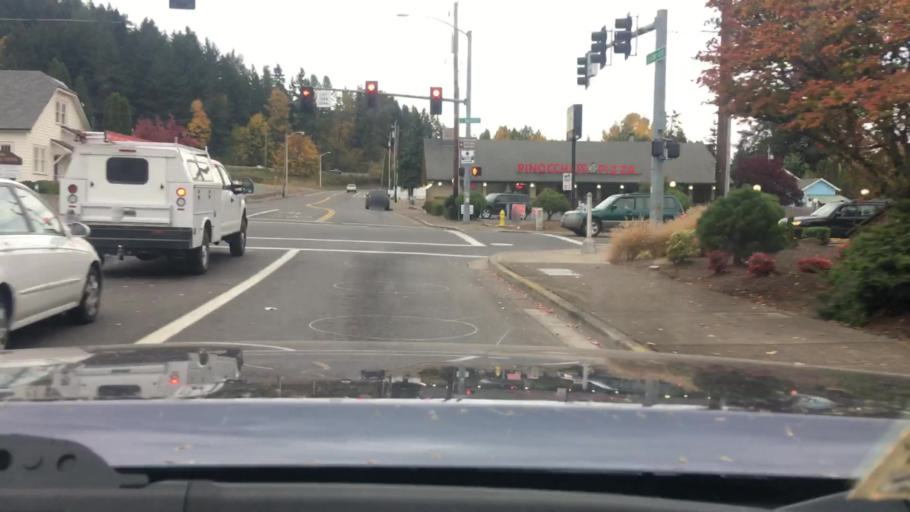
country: US
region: Oregon
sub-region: Lane County
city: Cottage Grove
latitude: 43.7975
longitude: -123.0488
